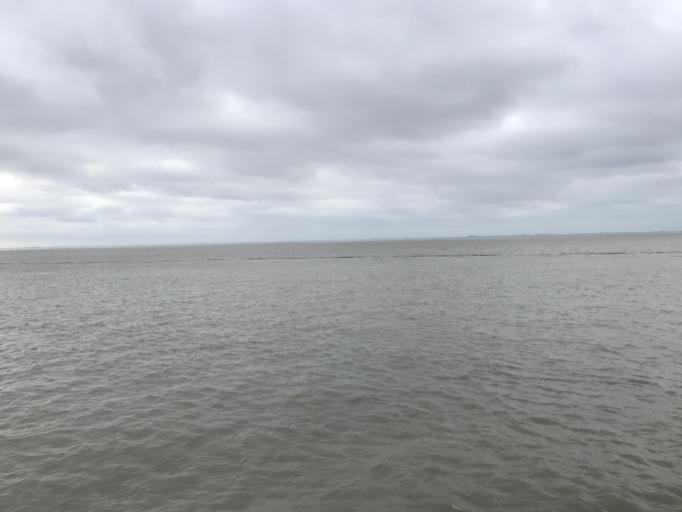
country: DE
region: Lower Saxony
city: Emden
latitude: 53.3304
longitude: 7.1162
